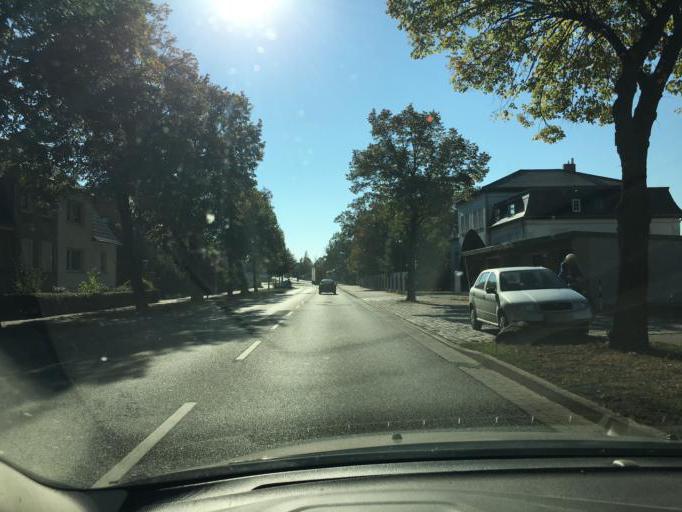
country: DE
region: Saxony-Anhalt
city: Forderstedt
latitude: 51.8942
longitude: 11.6327
